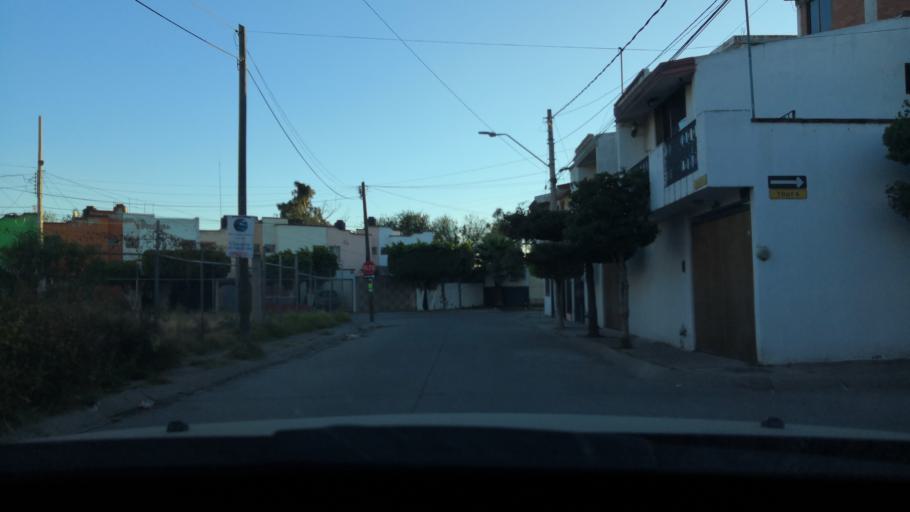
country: MX
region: Guanajuato
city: Leon
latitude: 21.1646
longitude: -101.6590
